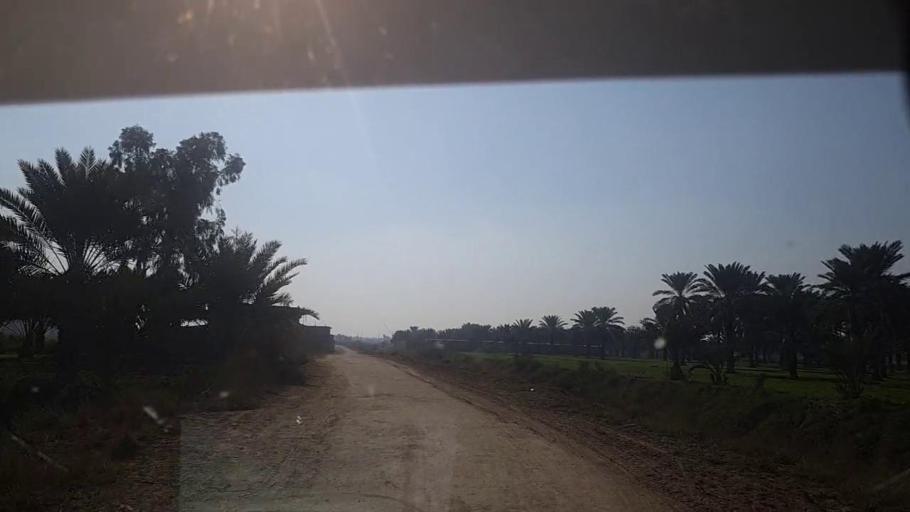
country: PK
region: Sindh
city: Gambat
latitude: 27.3663
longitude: 68.5598
